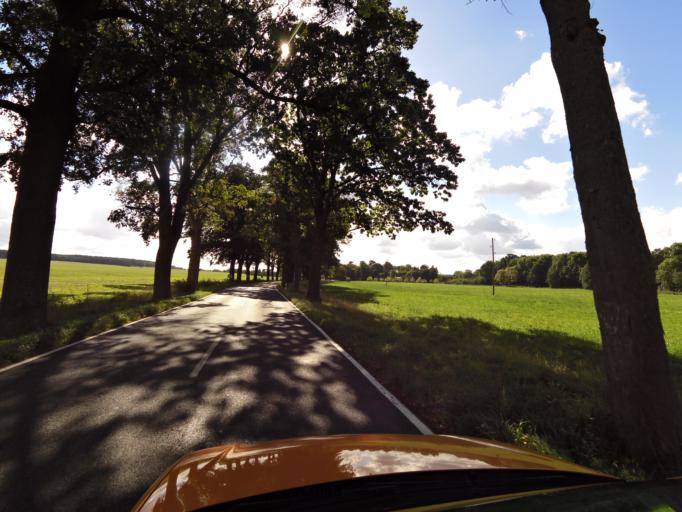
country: DE
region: Brandenburg
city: Michendorf
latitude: 52.2515
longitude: 13.0807
